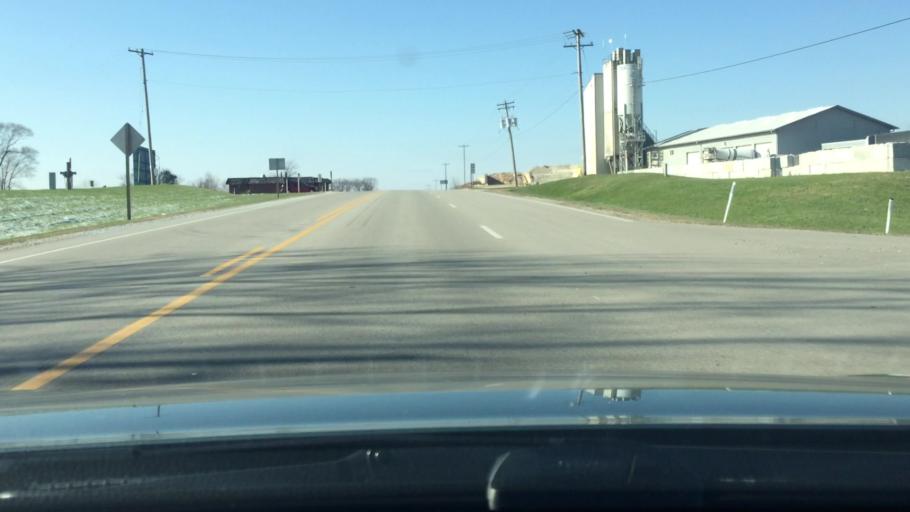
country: US
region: Wisconsin
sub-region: Jefferson County
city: Jefferson
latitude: 43.0068
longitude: -88.8455
